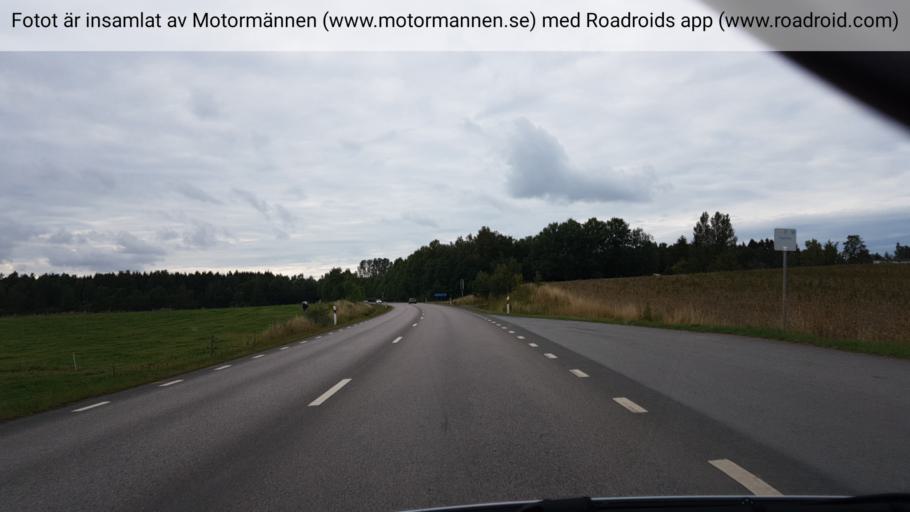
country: SE
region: Vaestra Goetaland
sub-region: Hjo Kommun
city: Hjo
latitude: 58.3325
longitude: 14.2530
